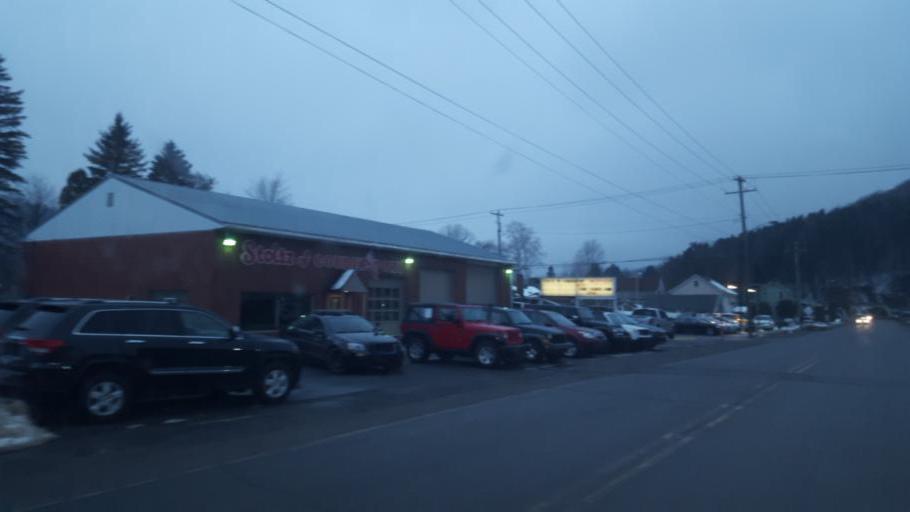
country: US
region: Pennsylvania
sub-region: Potter County
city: Coudersport
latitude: 41.7697
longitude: -78.0219
